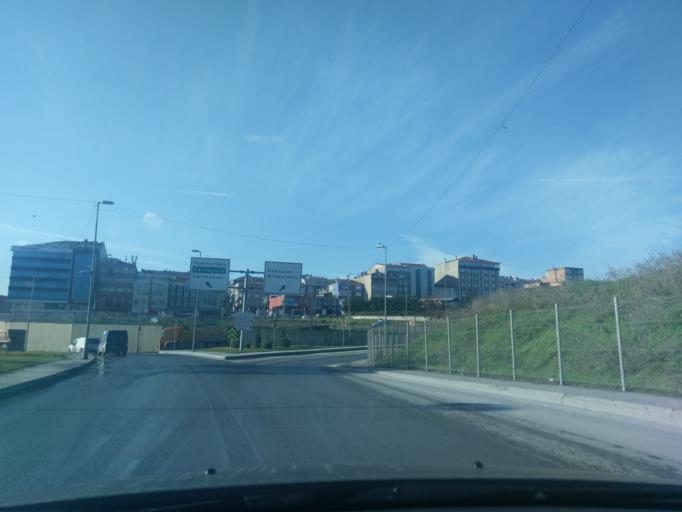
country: TR
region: Istanbul
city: Sultangazi
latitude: 41.1171
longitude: 28.8530
